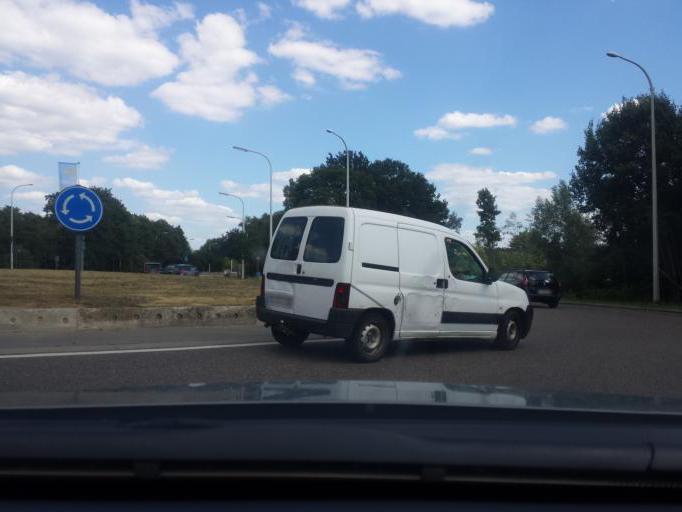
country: BE
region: Flanders
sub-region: Provincie Limburg
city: Beringen
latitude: 51.0359
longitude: 5.2445
